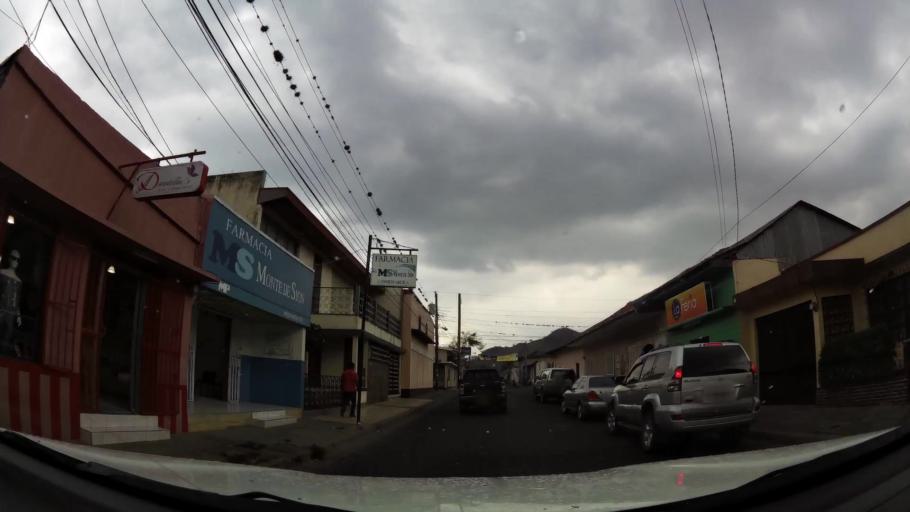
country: NI
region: Jinotega
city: Jinotega
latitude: 13.0902
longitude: -86.0028
